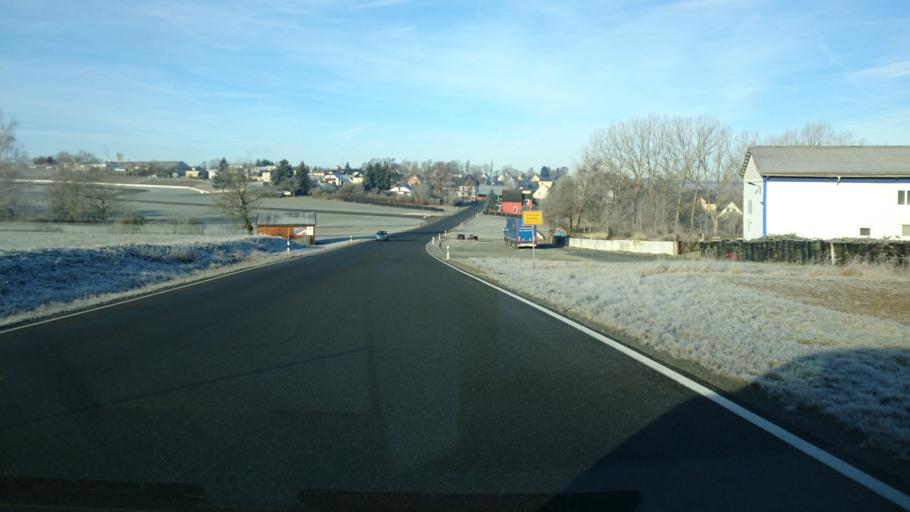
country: DE
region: Thuringia
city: Schleiz
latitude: 50.5676
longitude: 11.8148
